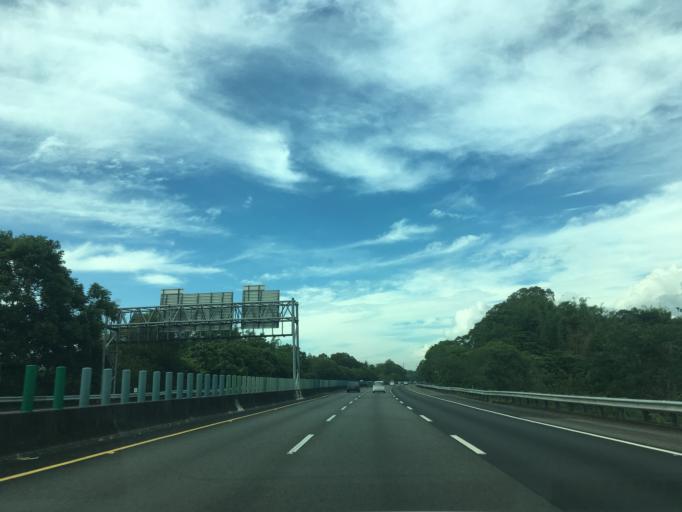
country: TW
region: Taiwan
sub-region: Chiayi
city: Jiayi Shi
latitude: 23.5318
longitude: 120.4884
